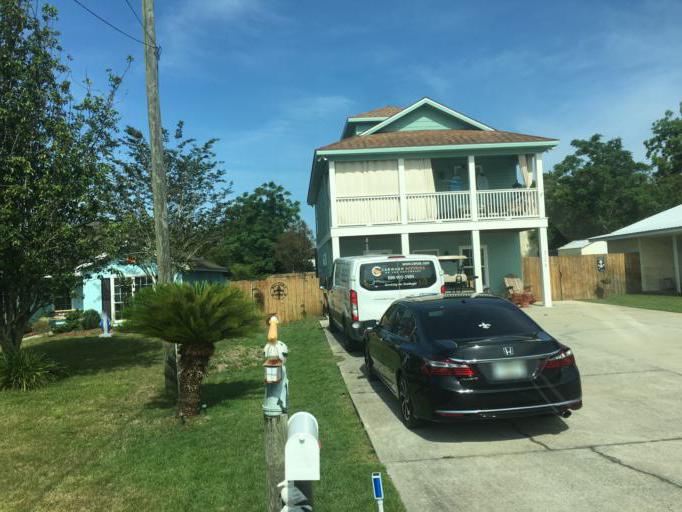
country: US
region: Florida
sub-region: Bay County
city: Laguna Beach
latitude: 30.2590
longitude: -85.9610
